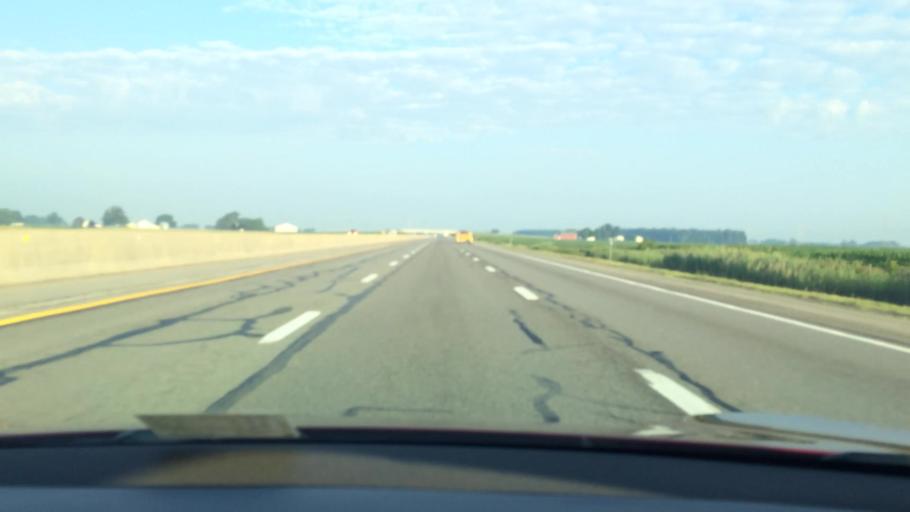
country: US
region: Ohio
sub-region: Erie County
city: Milan
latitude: 41.3317
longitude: -82.6622
